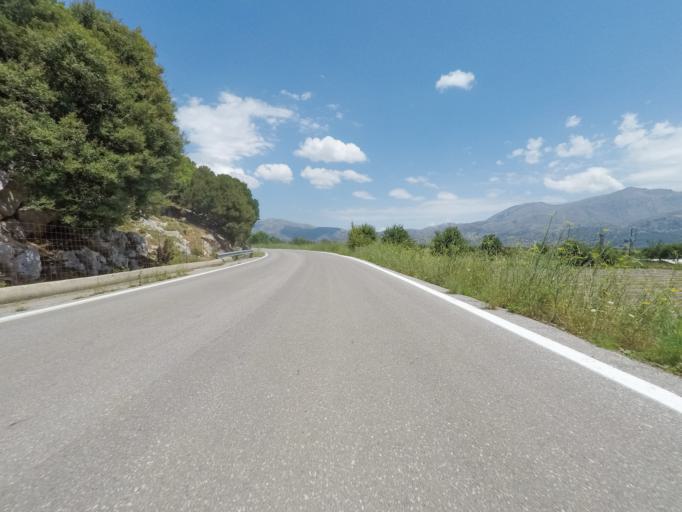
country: GR
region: Crete
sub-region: Nomos Irakleiou
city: Mokhos
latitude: 35.1964
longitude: 25.4561
